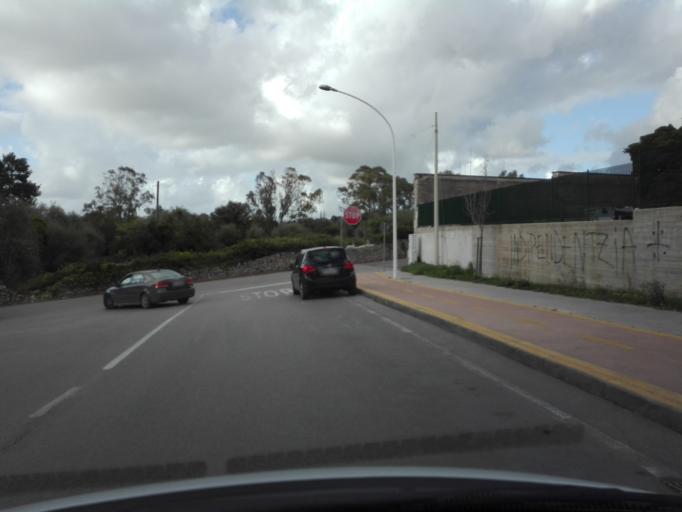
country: IT
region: Sardinia
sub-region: Provincia di Sassari
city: Sassari
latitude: 40.7158
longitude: 8.5843
